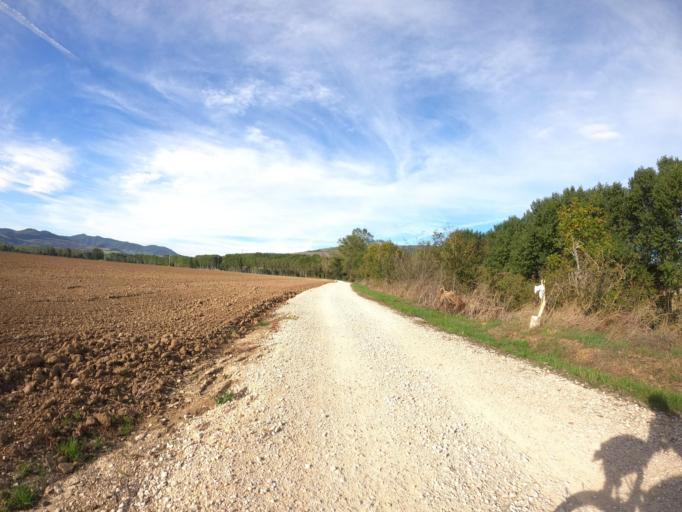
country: ES
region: Navarre
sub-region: Provincia de Navarra
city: Oltza
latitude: 42.8089
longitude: -1.7644
